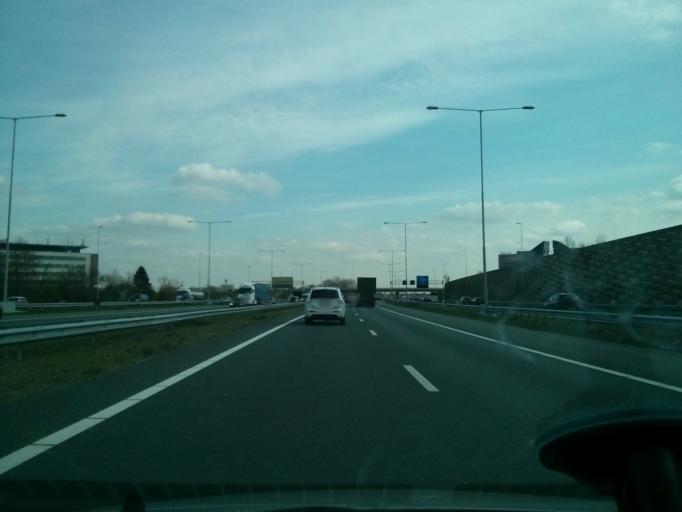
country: NL
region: North Brabant
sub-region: Gemeente 's-Hertogenbosch
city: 's-Hertogenbosch
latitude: 51.7188
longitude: 5.3341
